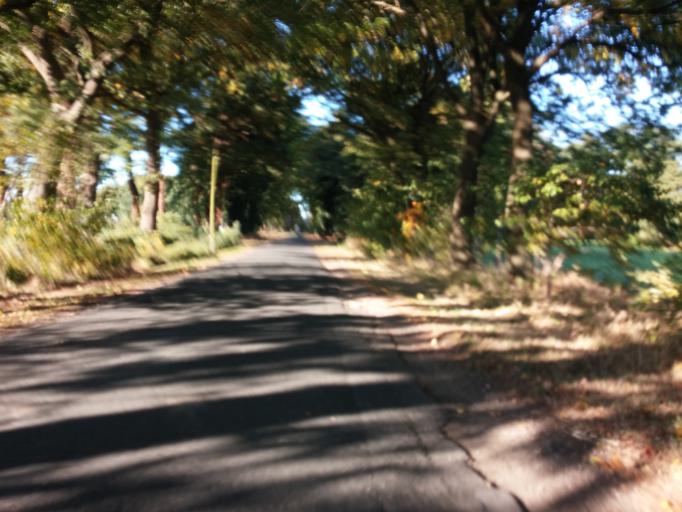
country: DE
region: North Rhine-Westphalia
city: Dorsten
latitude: 51.6402
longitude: 6.9777
